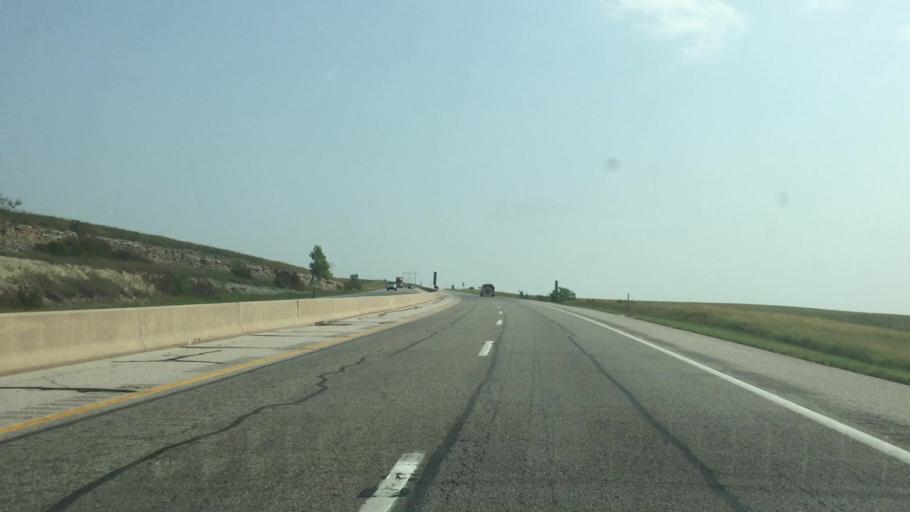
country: US
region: Kansas
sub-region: Chase County
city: Cottonwood Falls
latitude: 38.1785
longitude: -96.4641
